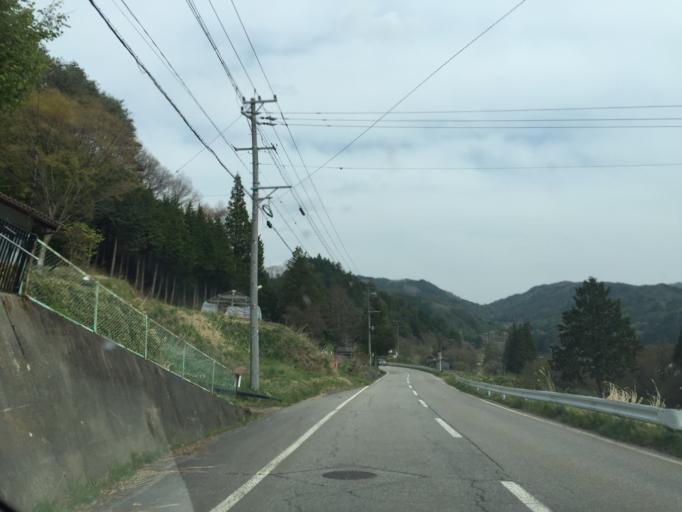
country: JP
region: Nagano
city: Iida
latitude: 35.2767
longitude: 137.7072
